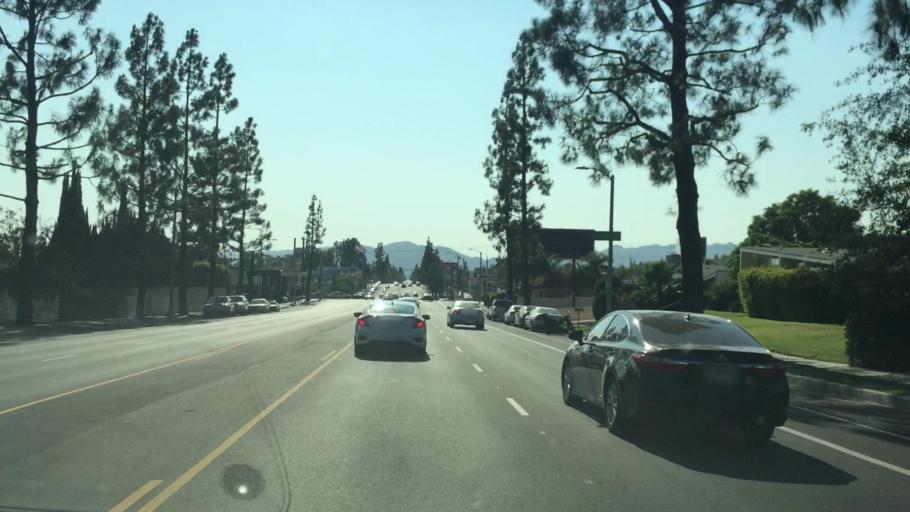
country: US
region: California
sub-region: Los Angeles County
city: Northridge
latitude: 34.2573
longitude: -118.5340
